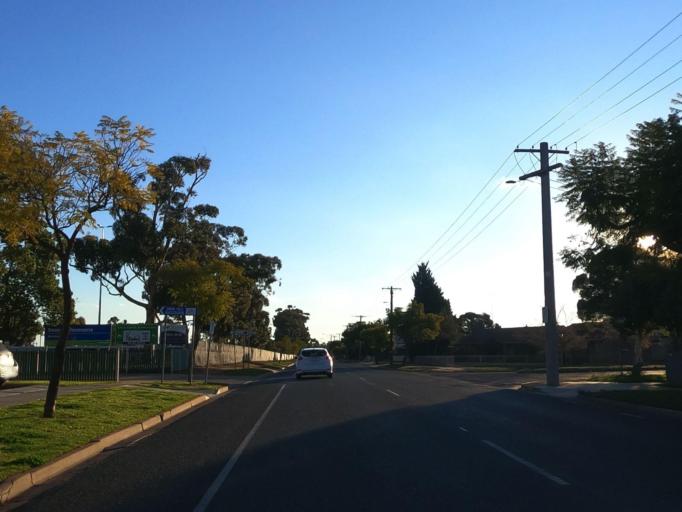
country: AU
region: Victoria
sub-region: Swan Hill
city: Swan Hill
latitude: -35.3481
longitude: 143.5595
